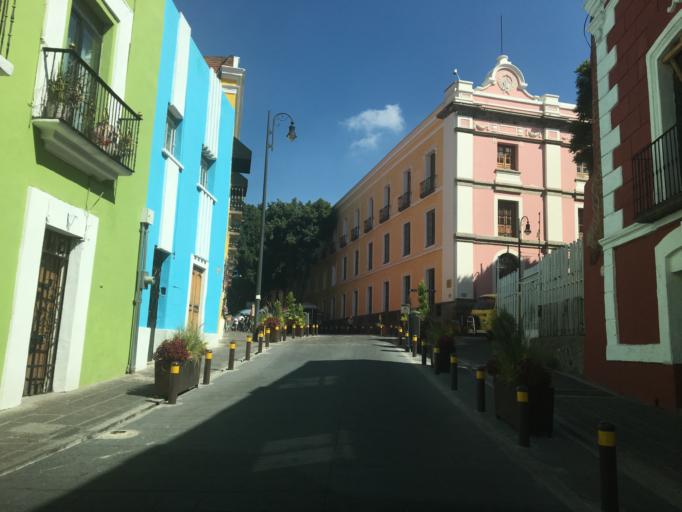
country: MX
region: Puebla
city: Puebla
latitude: 19.0413
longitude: -98.1947
